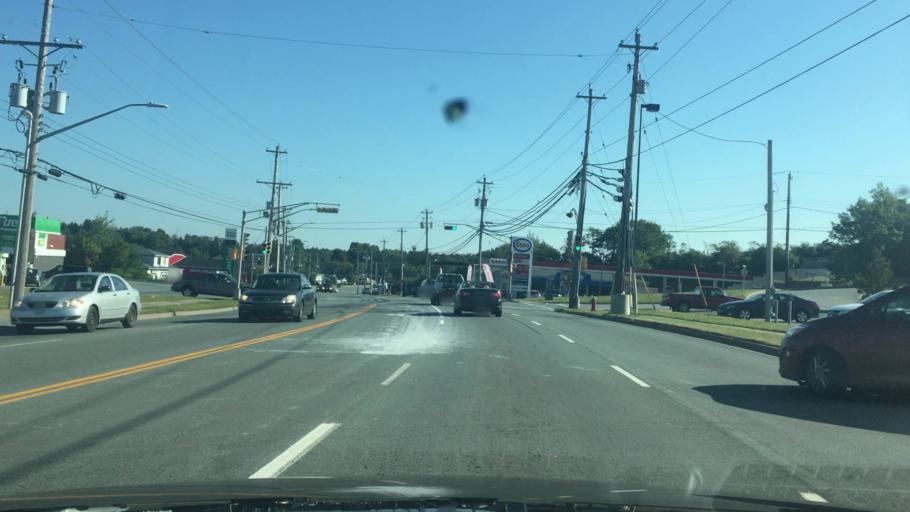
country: CA
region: Nova Scotia
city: Cole Harbour
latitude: 44.6943
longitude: -63.4979
